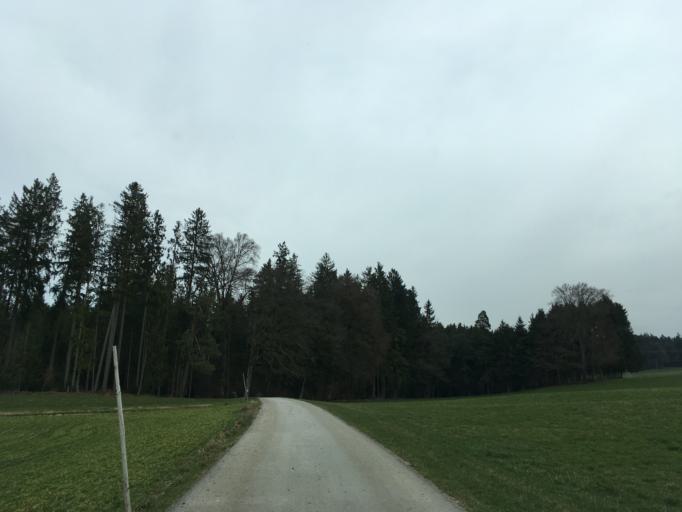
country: DE
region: Bavaria
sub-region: Upper Bavaria
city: Schnaitsee
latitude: 48.0584
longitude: 12.3752
